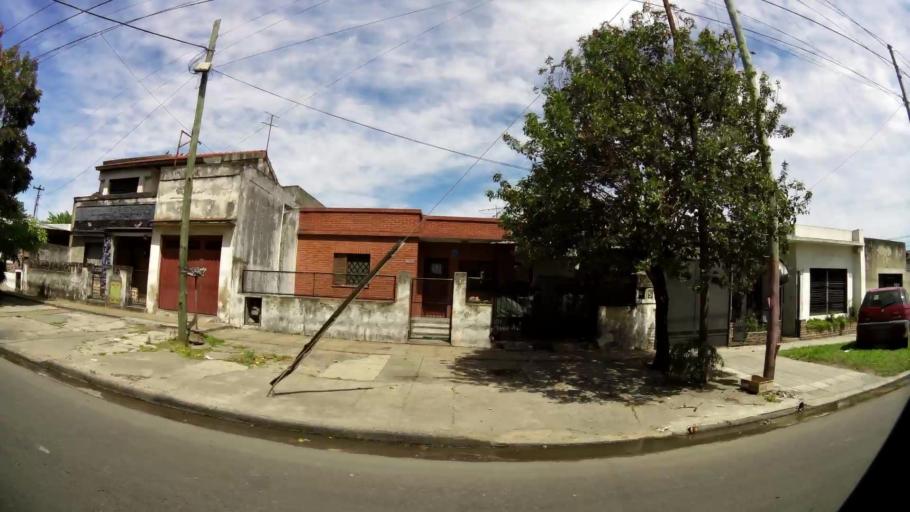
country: AR
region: Buenos Aires
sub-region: Partido de Quilmes
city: Quilmes
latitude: -34.7564
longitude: -58.2964
